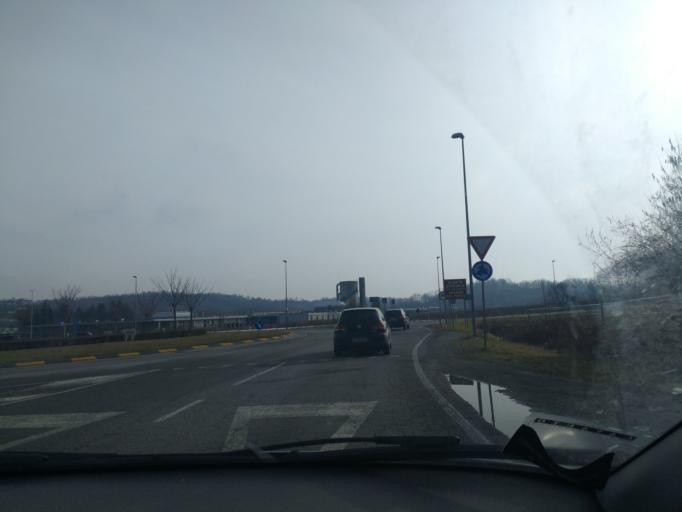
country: IT
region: Lombardy
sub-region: Provincia di Como
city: Anzano del Parco
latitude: 45.7634
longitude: 9.2029
